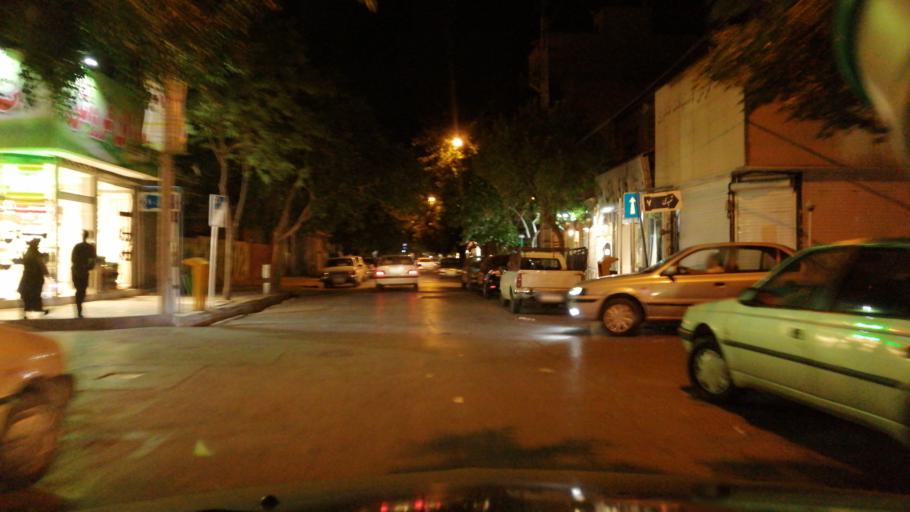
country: IR
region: Razavi Khorasan
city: Mashhad
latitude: 36.3063
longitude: 59.5989
